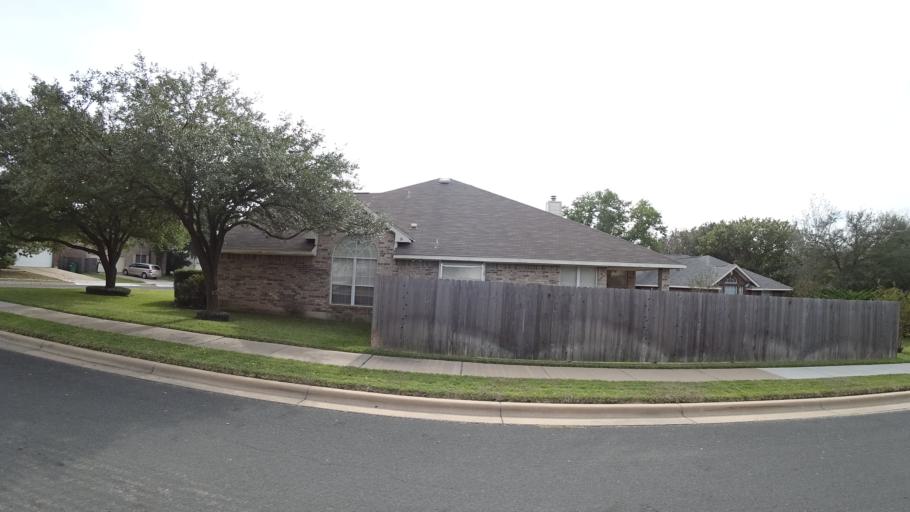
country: US
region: Texas
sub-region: Travis County
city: Wells Branch
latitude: 30.4532
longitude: -97.6794
